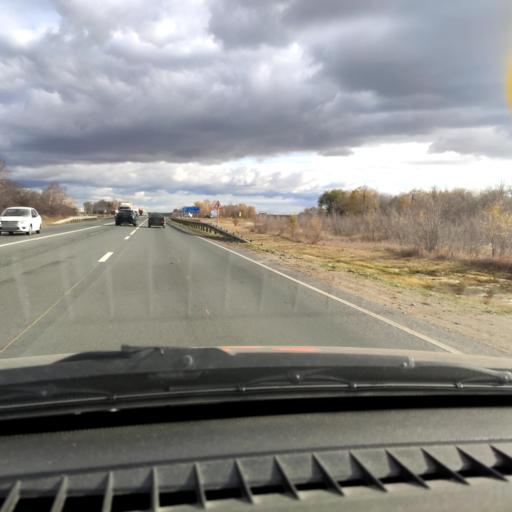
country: RU
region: Samara
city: Syzran'
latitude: 53.2124
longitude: 48.5513
